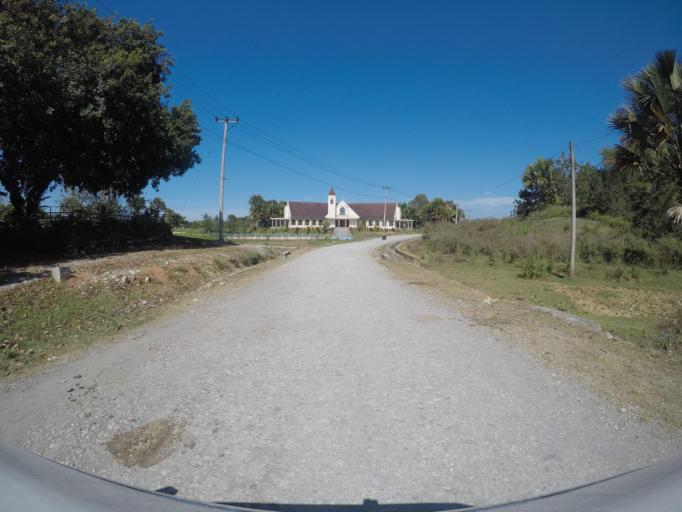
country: TL
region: Viqueque
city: Viqueque
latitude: -8.9752
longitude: 126.0510
